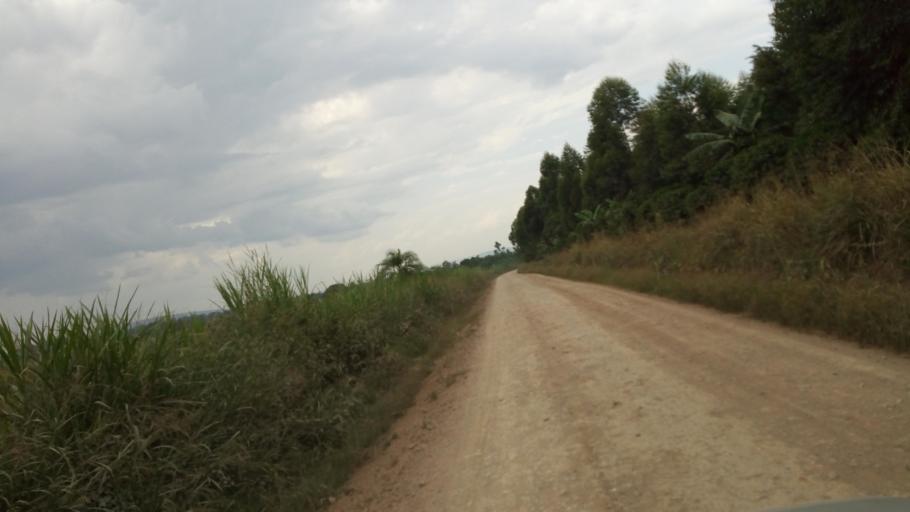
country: UG
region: Central Region
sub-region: Kiboga District
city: Kiboga
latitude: 0.7190
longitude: 31.7417
